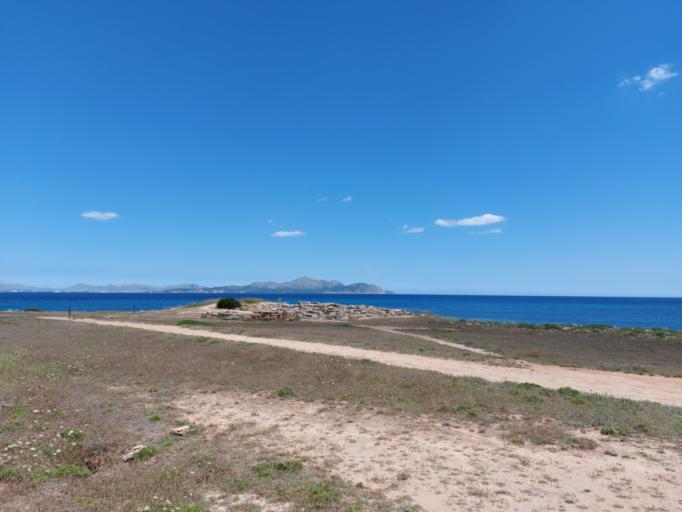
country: ES
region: Balearic Islands
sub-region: Illes Balears
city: Santa Margalida
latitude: 39.7543
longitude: 3.1823
